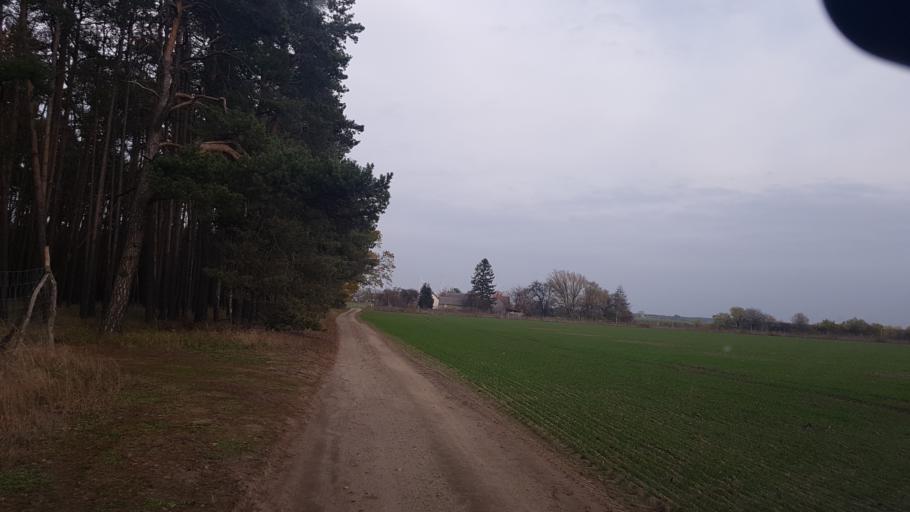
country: DE
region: Brandenburg
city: Schilda
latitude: 51.6590
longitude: 13.4041
